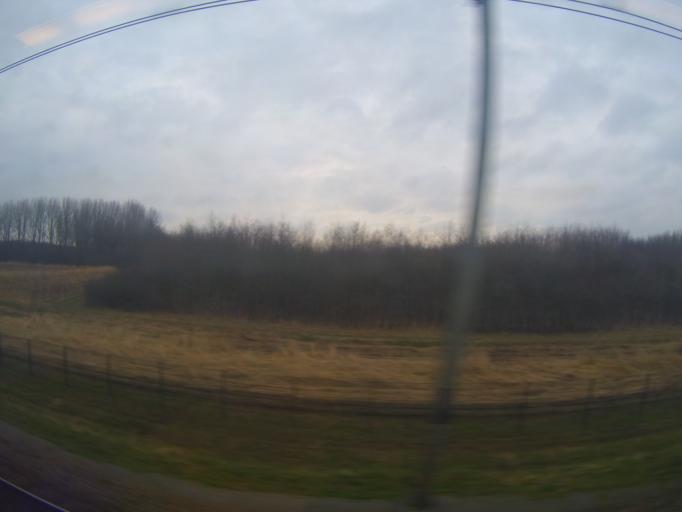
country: NL
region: South Holland
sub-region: Gemeente Pijnacker-Nootdorp
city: Pijnacker
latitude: 52.0496
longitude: 4.4504
